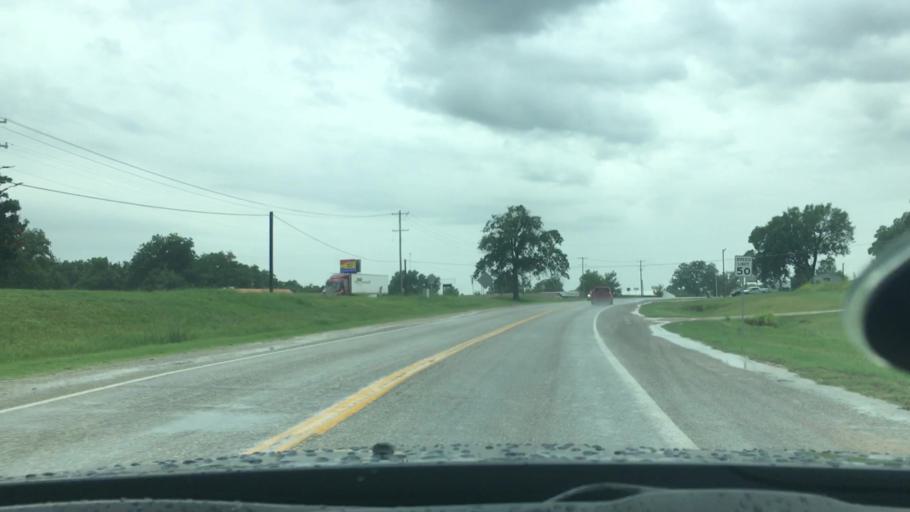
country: US
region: Oklahoma
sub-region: Johnston County
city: Tishomingo
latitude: 34.2380
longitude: -96.6972
